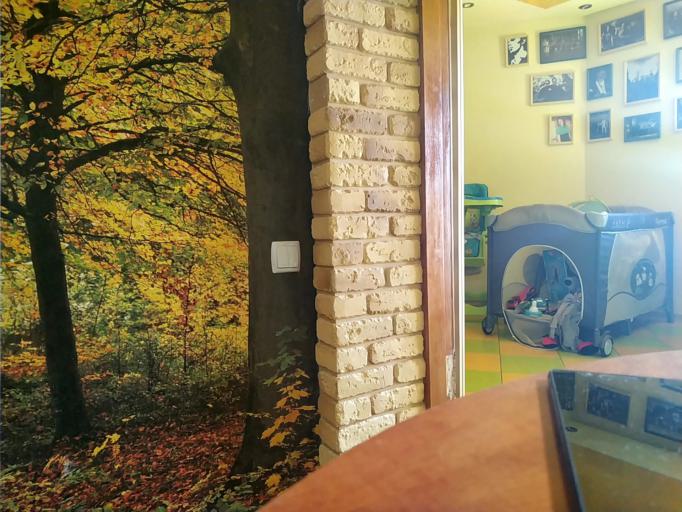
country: RU
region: Tverskaya
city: Vyshniy Volochek
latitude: 57.5889
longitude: 34.5686
